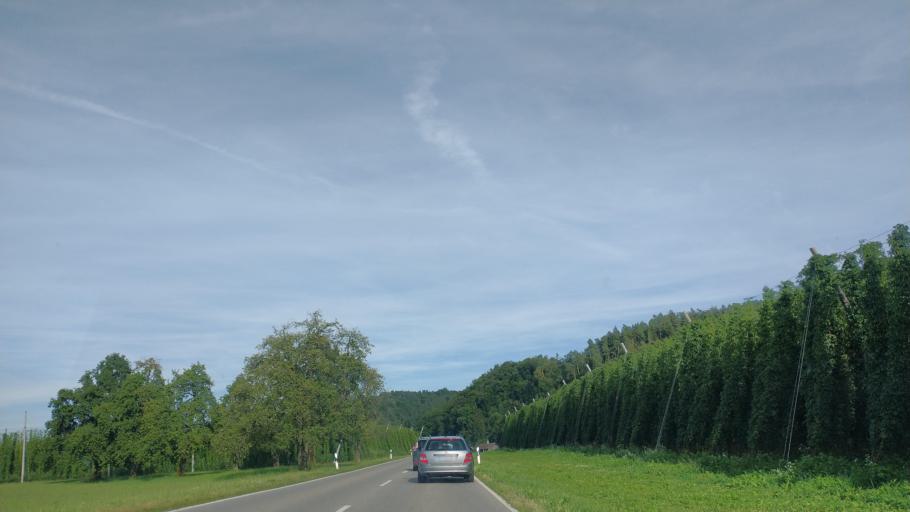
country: DE
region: Baden-Wuerttemberg
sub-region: Tuebingen Region
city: Kressbronn am Bodensee
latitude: 47.6261
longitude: 9.6065
